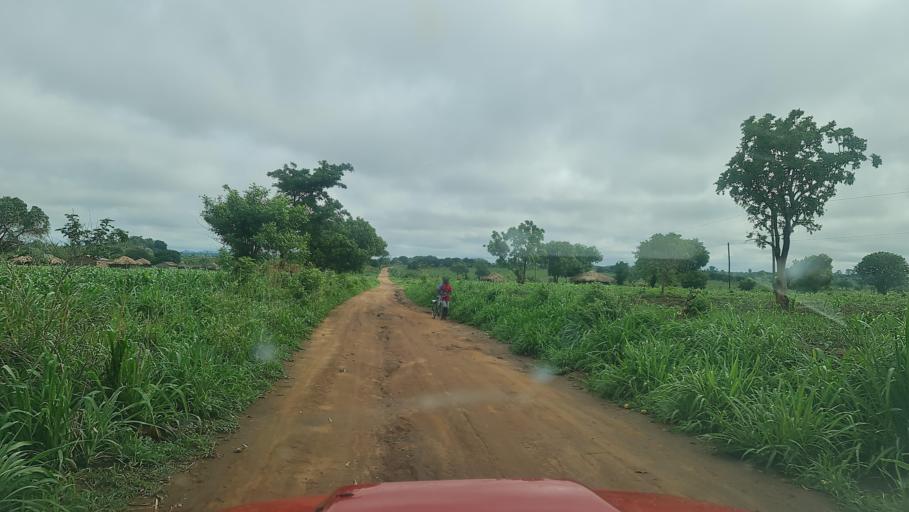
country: MW
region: Southern Region
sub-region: Nsanje District
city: Nsanje
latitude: -17.2095
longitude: 35.6794
